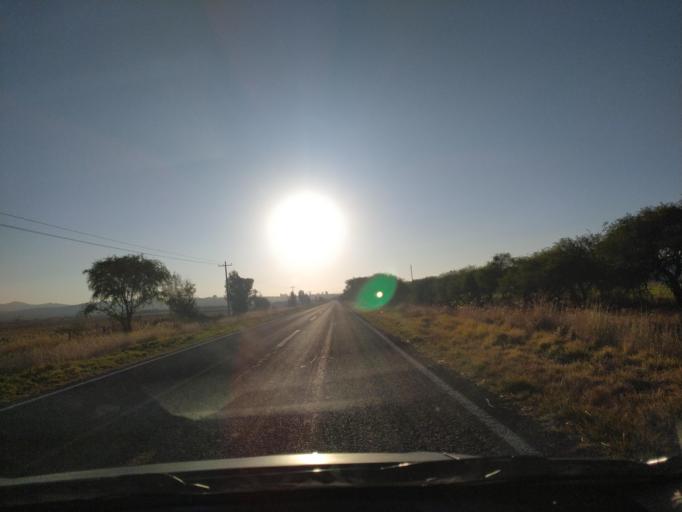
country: MX
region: Guanajuato
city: Ciudad Manuel Doblado
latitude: 20.7357
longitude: -101.8455
